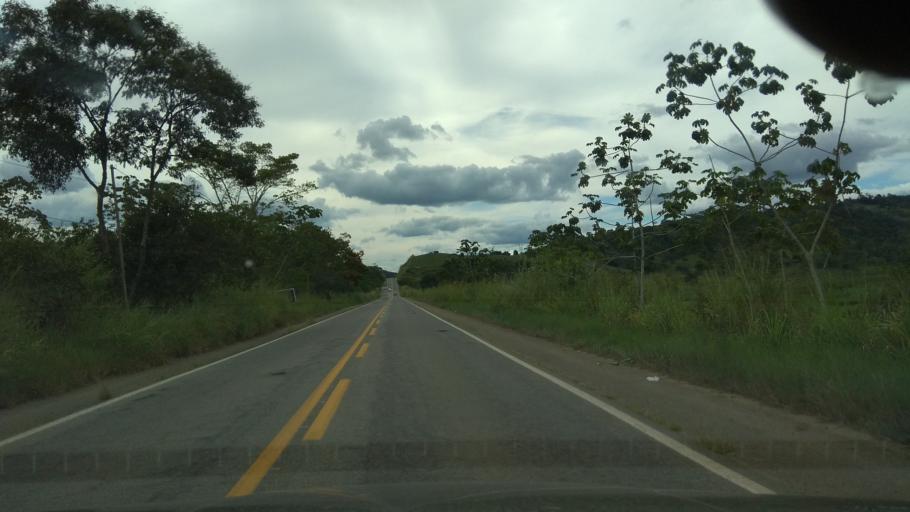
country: BR
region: Bahia
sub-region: Ipiau
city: Ipiau
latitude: -14.1597
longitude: -39.6929
